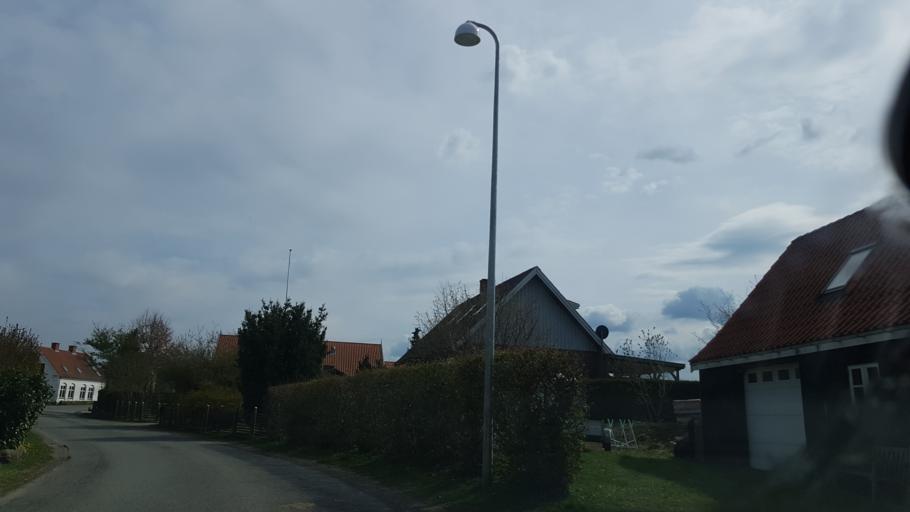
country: DK
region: Capital Region
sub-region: Allerod Kommune
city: Lillerod
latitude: 55.8946
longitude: 12.3275
